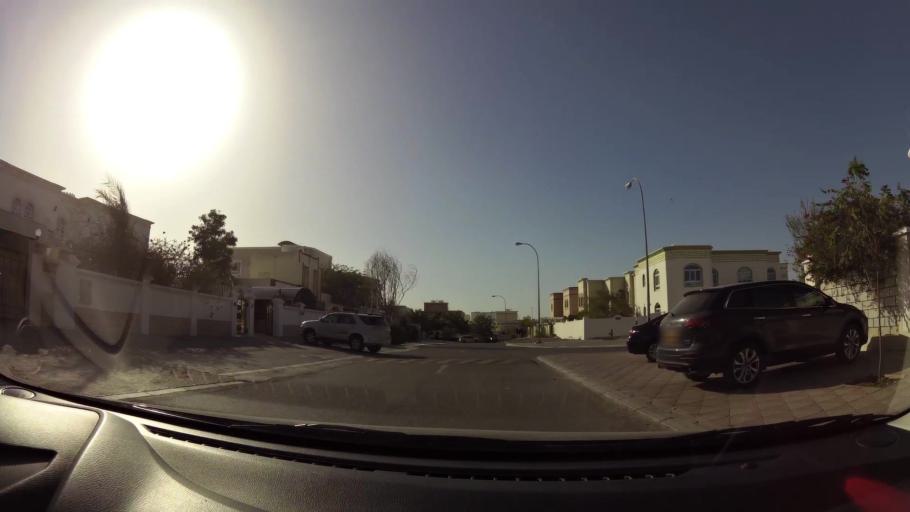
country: OM
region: Muhafazat Masqat
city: As Sib al Jadidah
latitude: 23.5988
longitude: 58.2131
